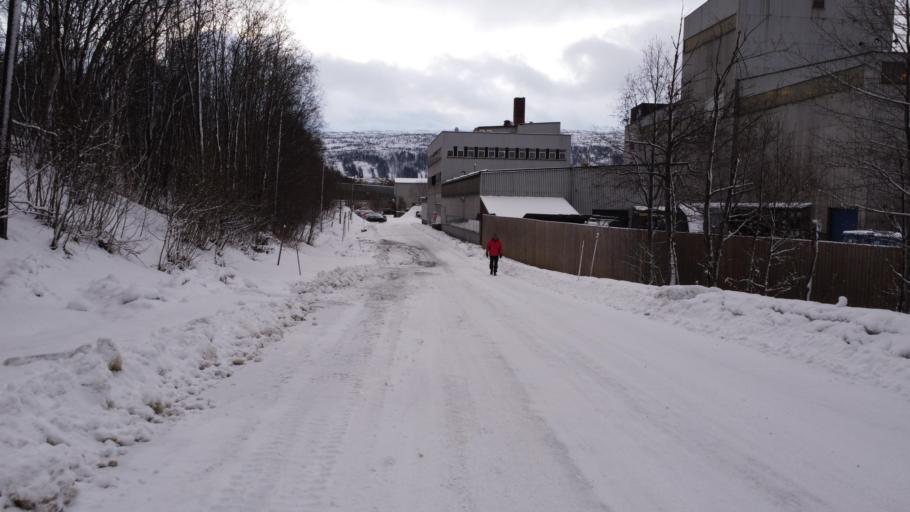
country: NO
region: Nordland
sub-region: Rana
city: Mo i Rana
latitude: 66.3279
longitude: 14.1516
